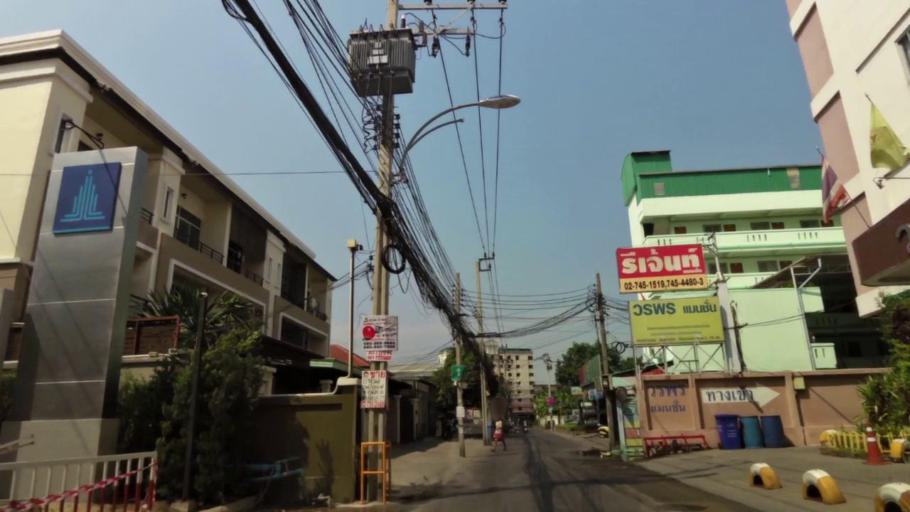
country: TH
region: Bangkok
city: Phra Khanong
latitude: 13.6550
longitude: 100.5944
